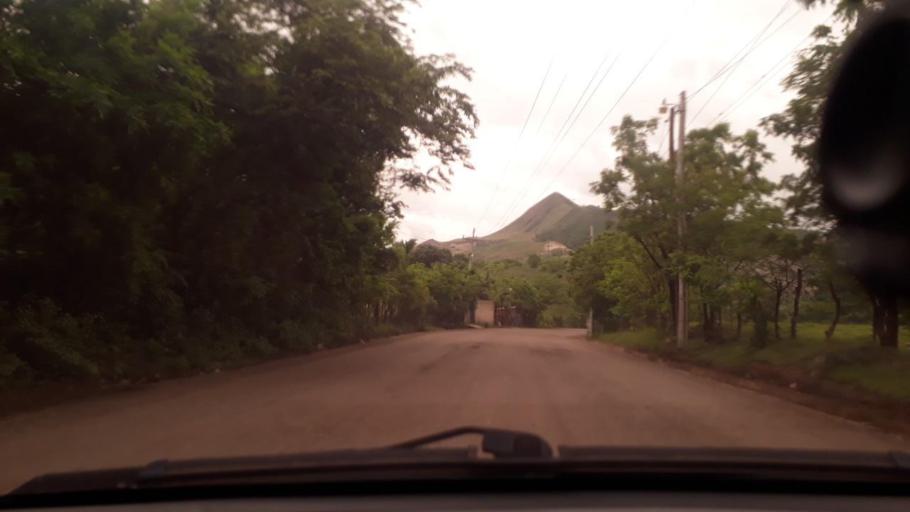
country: GT
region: Chiquimula
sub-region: Municipio de San Juan Ermita
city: San Juan Ermita
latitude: 14.7708
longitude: -89.4239
